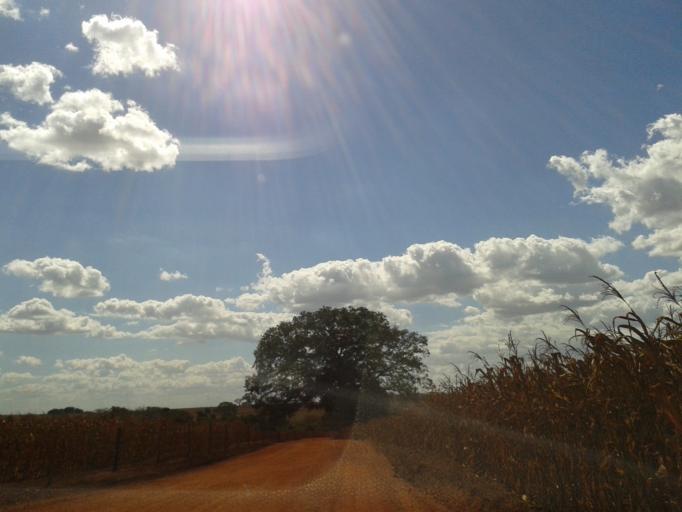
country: BR
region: Minas Gerais
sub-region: Capinopolis
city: Capinopolis
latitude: -18.6155
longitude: -49.4949
